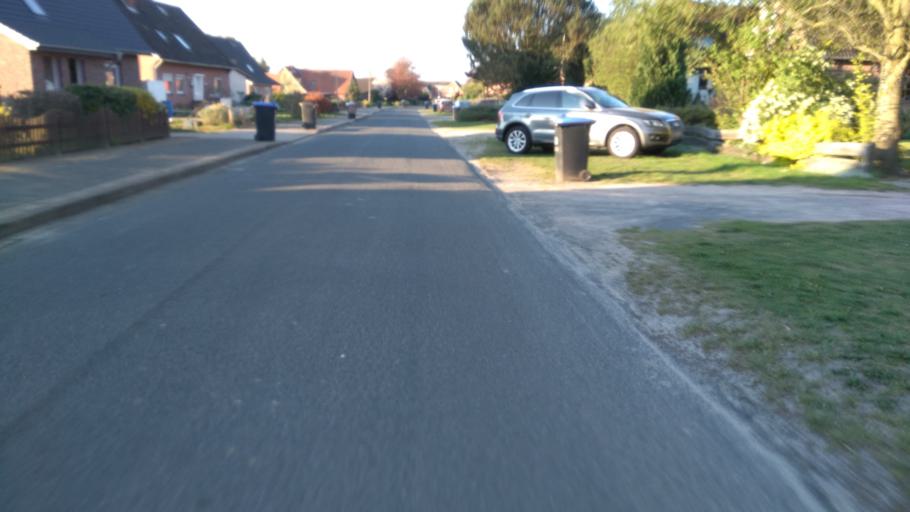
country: DE
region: Lower Saxony
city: Harsefeld
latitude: 53.4666
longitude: 9.5079
